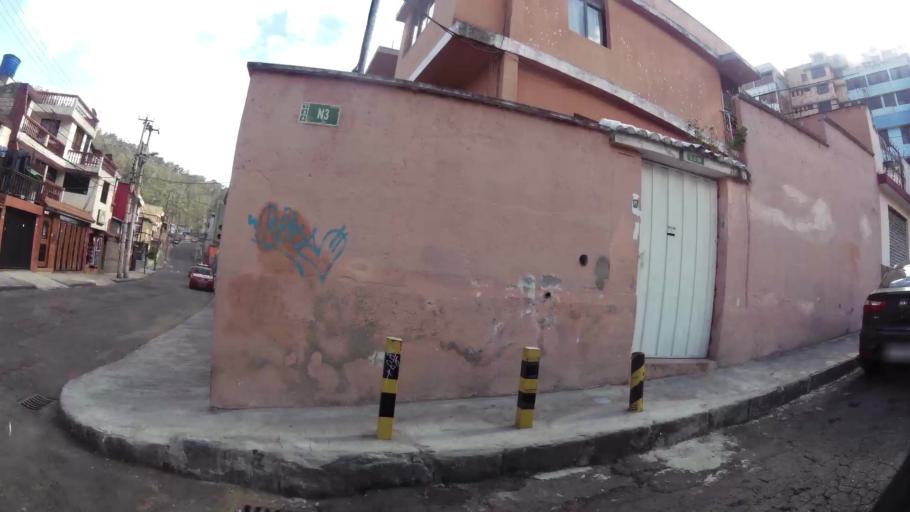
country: EC
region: Pichincha
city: Quito
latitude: -0.2282
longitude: -78.5015
